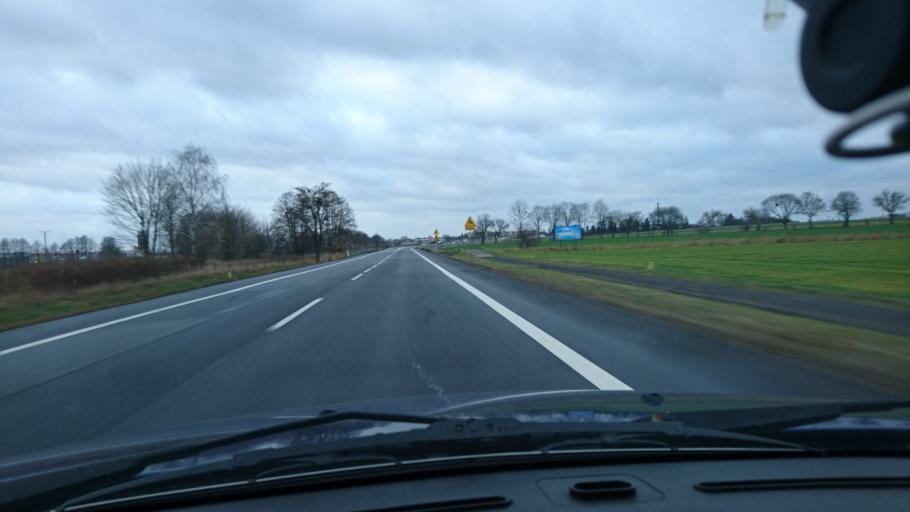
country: PL
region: Opole Voivodeship
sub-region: Powiat kluczborski
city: Kluczbork
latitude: 50.9908
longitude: 18.2199
